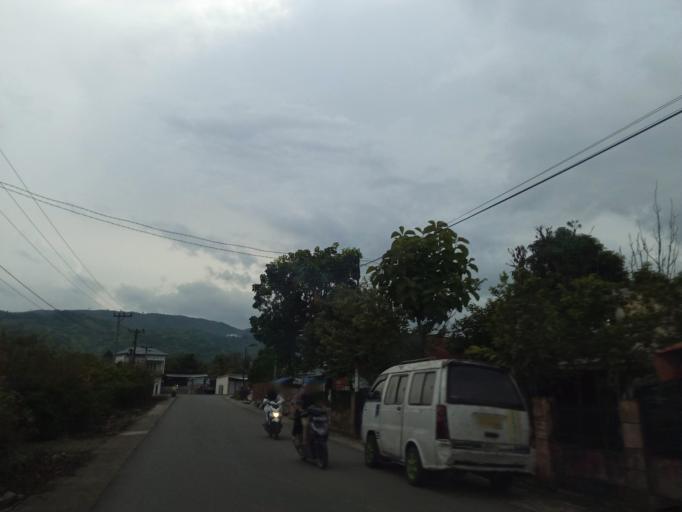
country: ID
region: Jambi
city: Semurup
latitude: -1.9888
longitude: 101.3603
